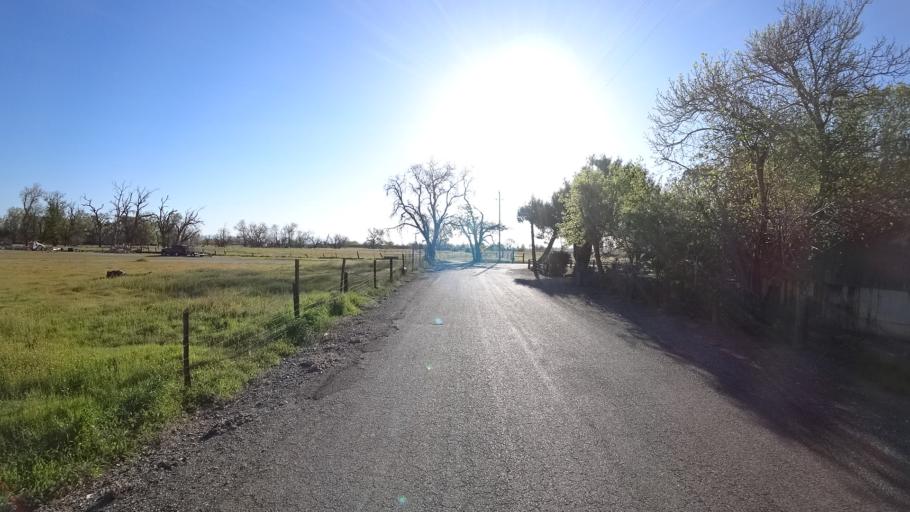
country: US
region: California
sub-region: Glenn County
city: Orland
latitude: 39.7693
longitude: -122.2160
